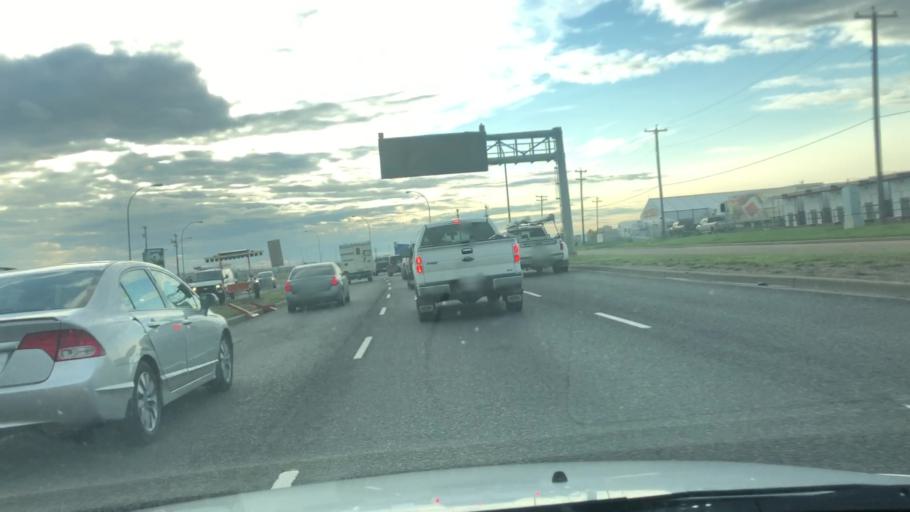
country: CA
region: Alberta
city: Edmonton
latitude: 53.5805
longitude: -113.5200
